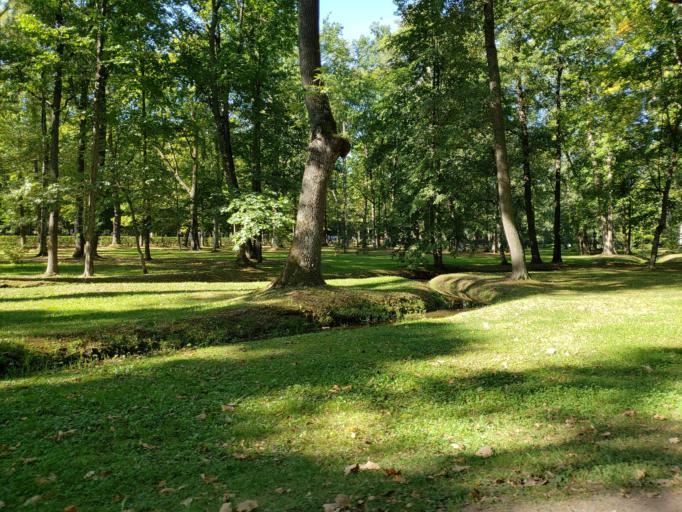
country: RU
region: St.-Petersburg
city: Peterhof
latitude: 59.8869
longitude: 29.9131
